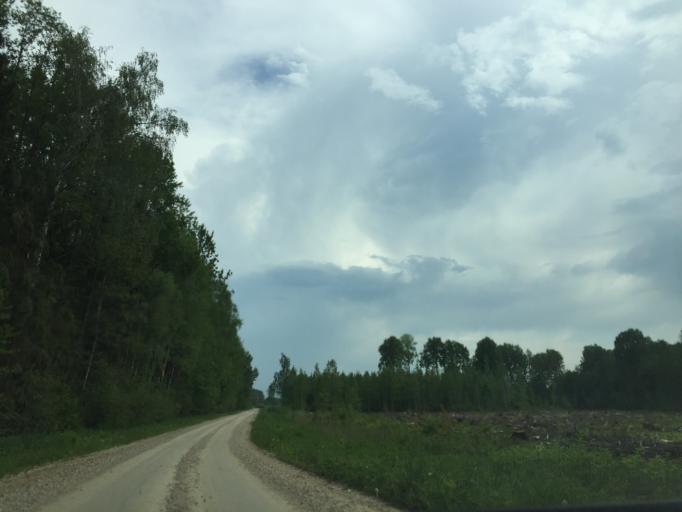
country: LV
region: Livani
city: Livani
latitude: 56.5575
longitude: 26.2237
